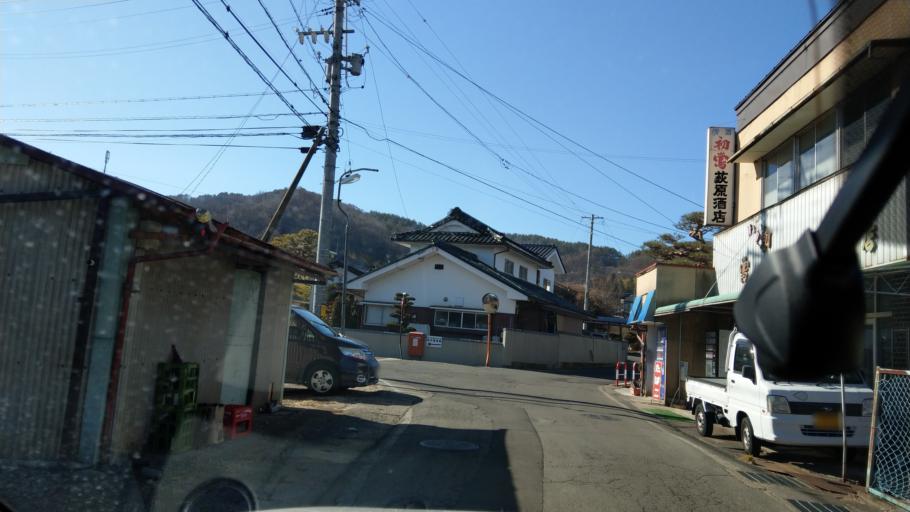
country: JP
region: Nagano
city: Saku
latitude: 36.2252
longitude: 138.4455
